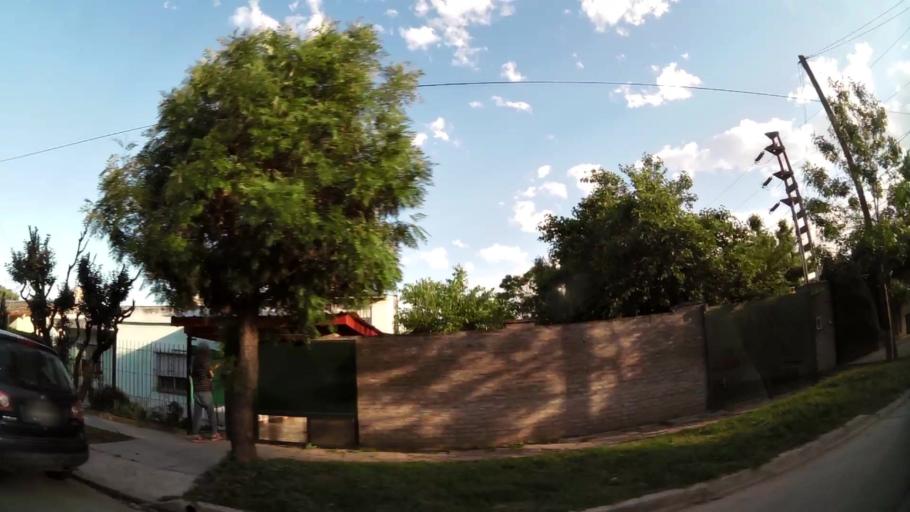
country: AR
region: Buenos Aires
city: Santa Catalina - Dique Lujan
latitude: -34.4736
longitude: -58.7502
